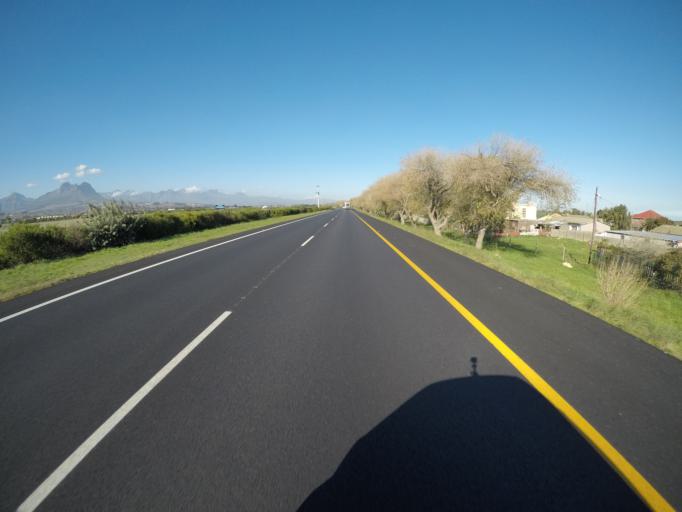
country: ZA
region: Western Cape
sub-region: Cape Winelands District Municipality
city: Stellenbosch
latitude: -34.0559
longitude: 18.7690
